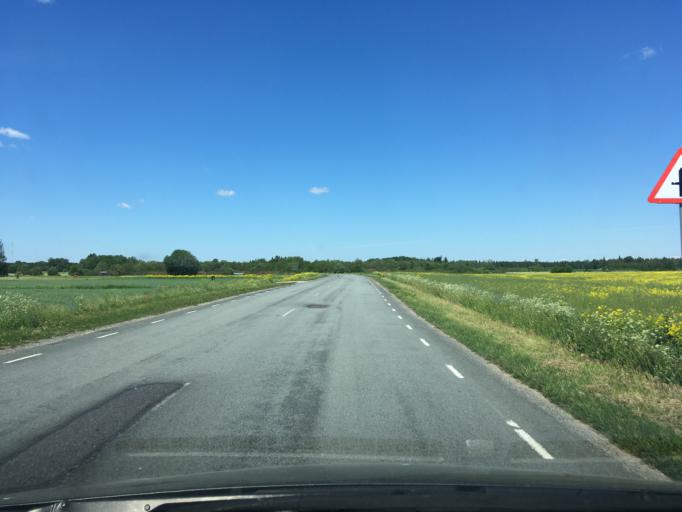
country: EE
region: Harju
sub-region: Rae vald
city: Vaida
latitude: 59.1871
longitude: 25.0091
